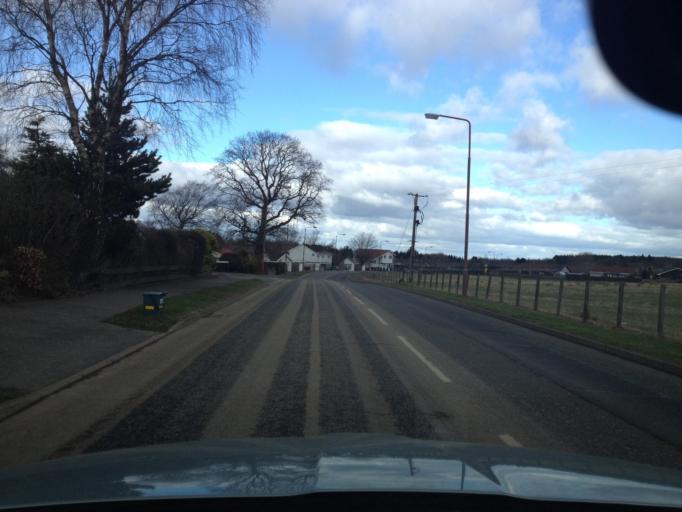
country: GB
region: Scotland
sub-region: West Lothian
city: Mid Calder
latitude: 55.8658
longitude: -3.5029
